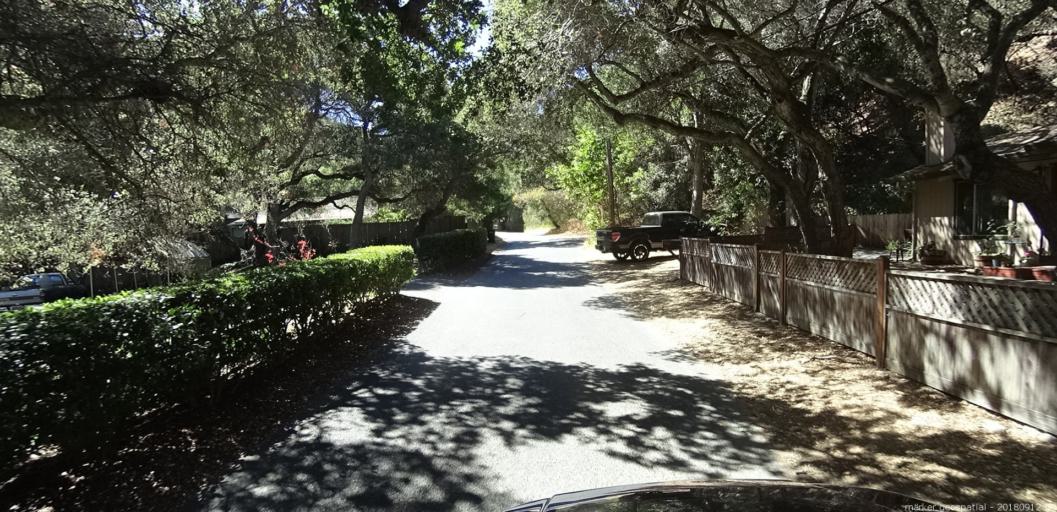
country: US
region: California
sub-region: Monterey County
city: Carmel Valley Village
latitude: 36.4688
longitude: -121.7237
